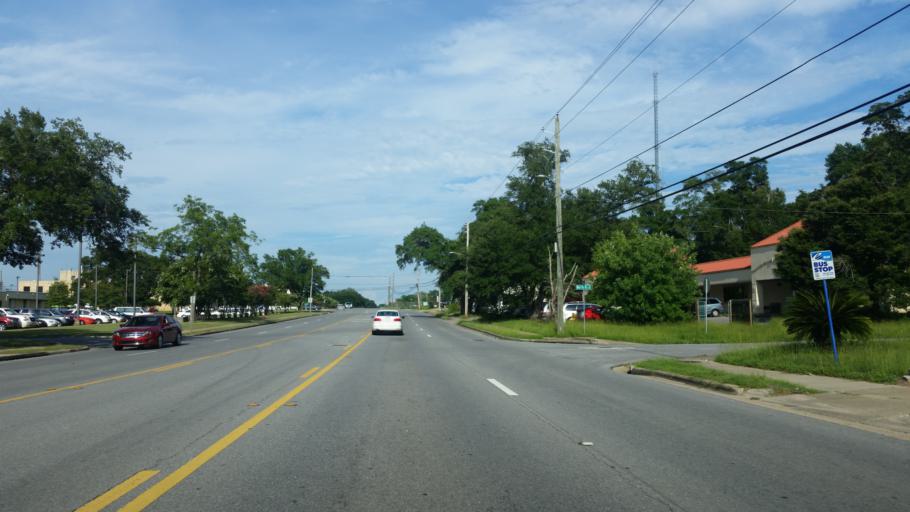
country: US
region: Florida
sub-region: Escambia County
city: Goulding
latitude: 30.4415
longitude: -87.2382
